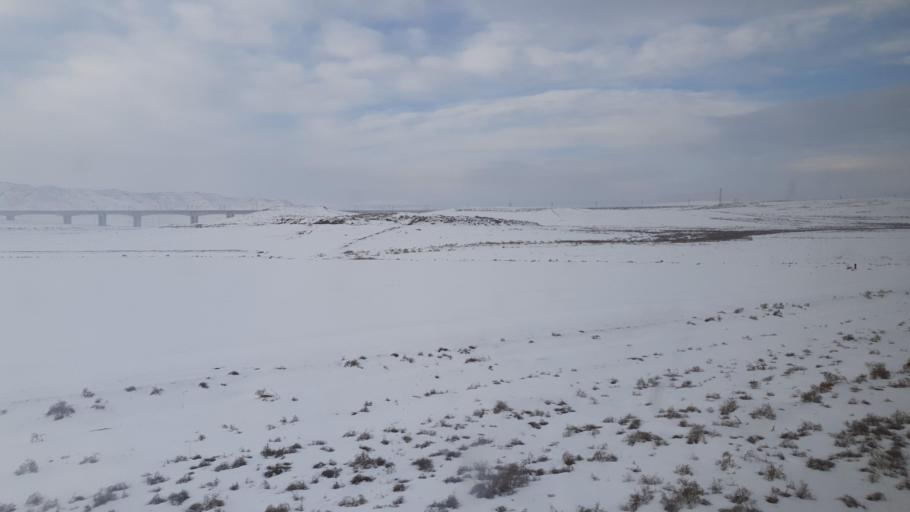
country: TR
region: Kirikkale
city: Delice
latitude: 39.8959
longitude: 33.9856
